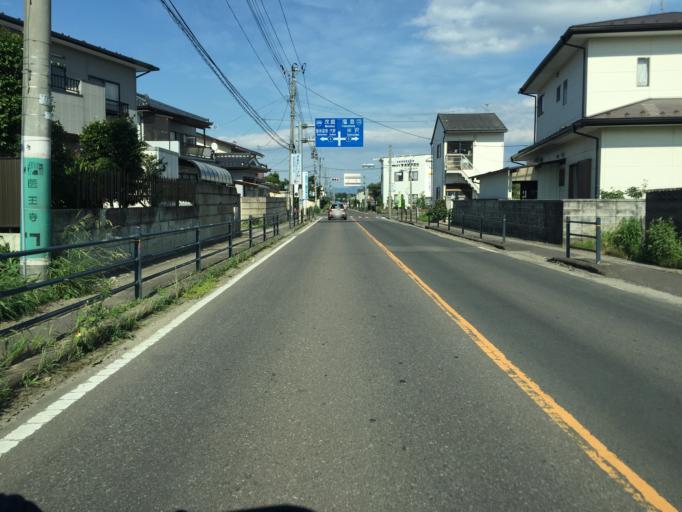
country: JP
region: Fukushima
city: Fukushima-shi
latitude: 37.8185
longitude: 140.4406
